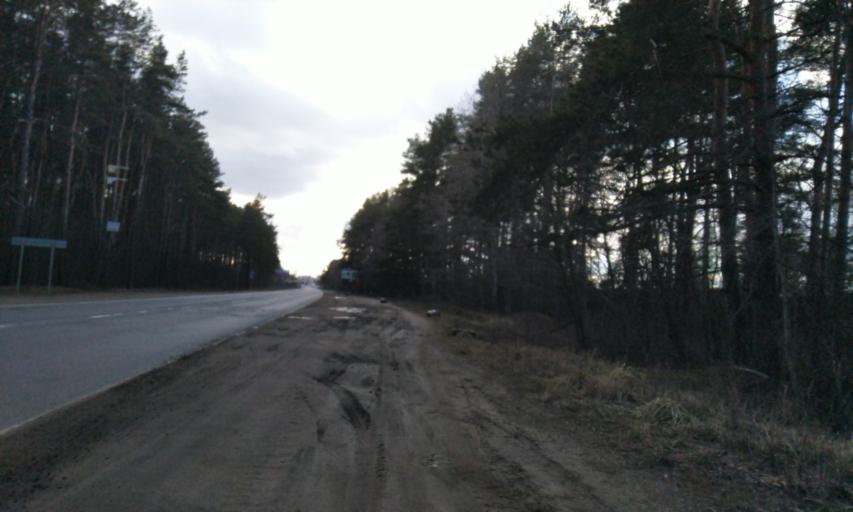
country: RU
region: Leningrad
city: Novoye Devyatkino
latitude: 60.1114
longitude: 30.4438
